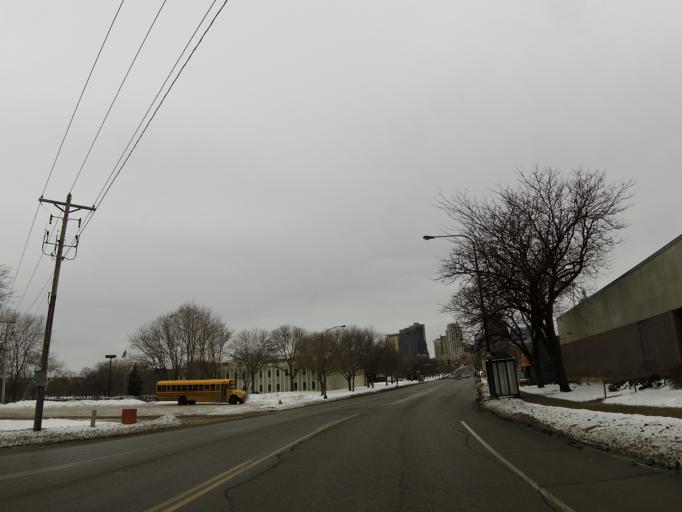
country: US
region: Minnesota
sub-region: Ramsey County
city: Saint Paul
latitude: 44.9359
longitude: -93.0864
